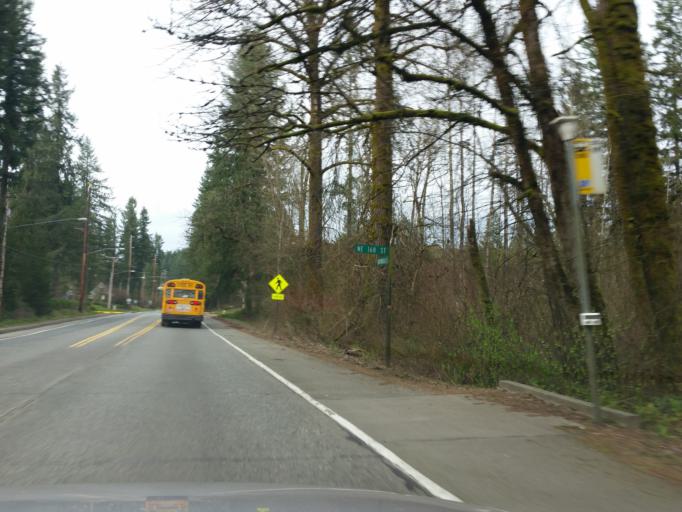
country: US
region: Washington
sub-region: King County
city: Cottage Lake
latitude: 47.7504
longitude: -122.0814
